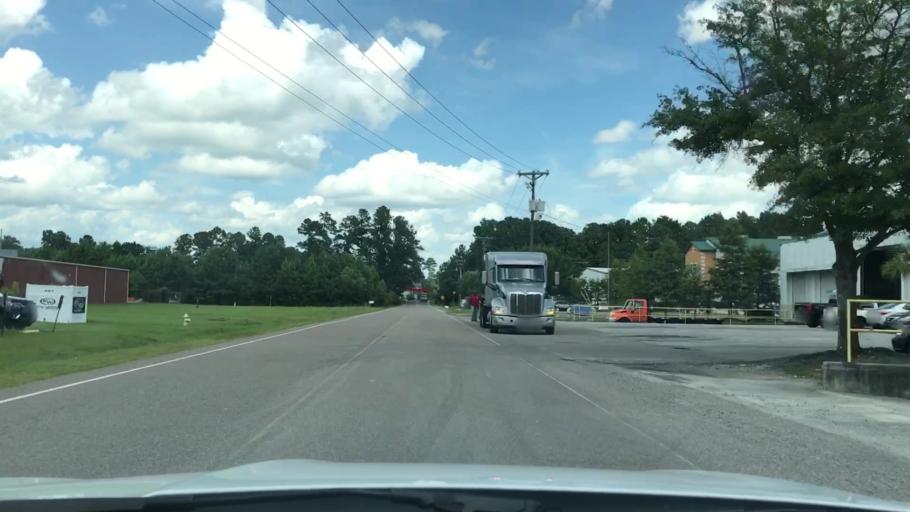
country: US
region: South Carolina
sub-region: Dorchester County
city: Summerville
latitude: 33.0346
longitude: -80.2067
